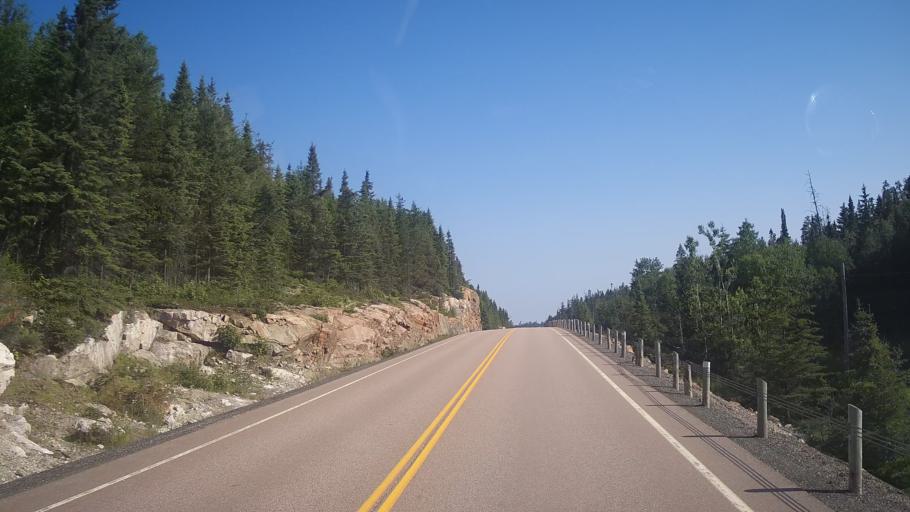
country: CA
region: Ontario
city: Rayside-Balfour
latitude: 46.9990
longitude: -81.6324
